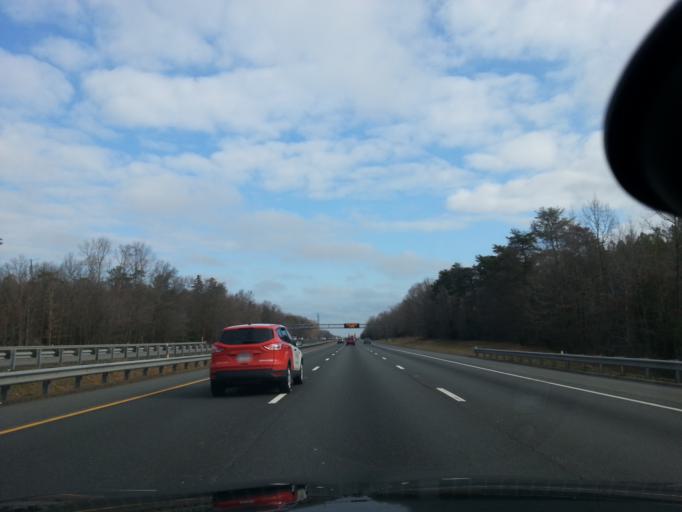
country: US
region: Virginia
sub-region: Spotsylvania County
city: Spotsylvania Courthouse
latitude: 38.1830
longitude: -77.5014
